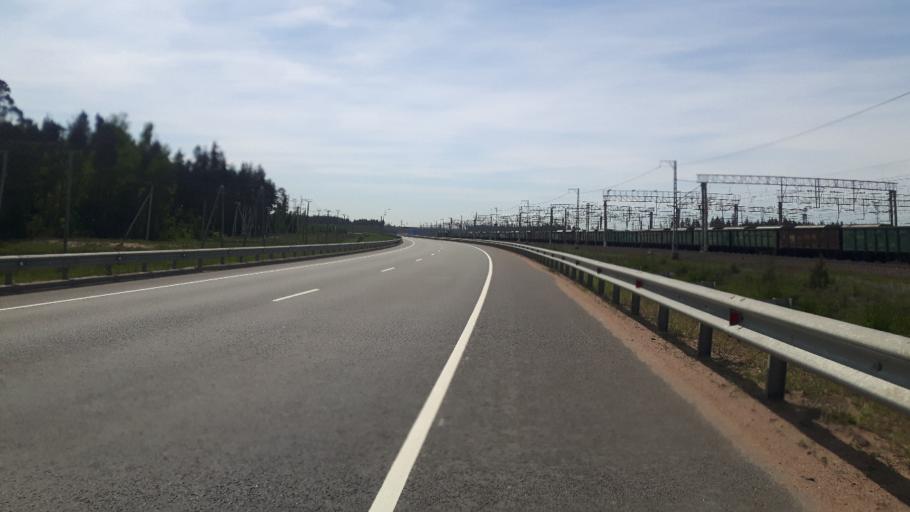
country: RU
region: Leningrad
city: Vistino
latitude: 59.6707
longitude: 28.4328
